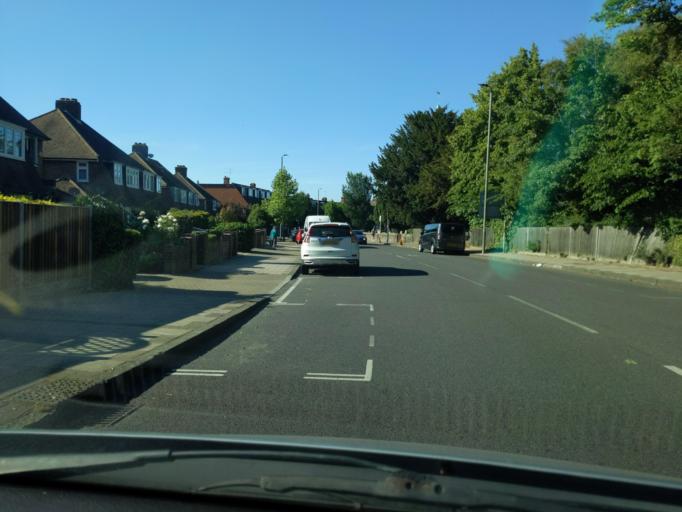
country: GB
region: England
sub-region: Greater London
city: Bromley
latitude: 51.3776
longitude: 0.0176
